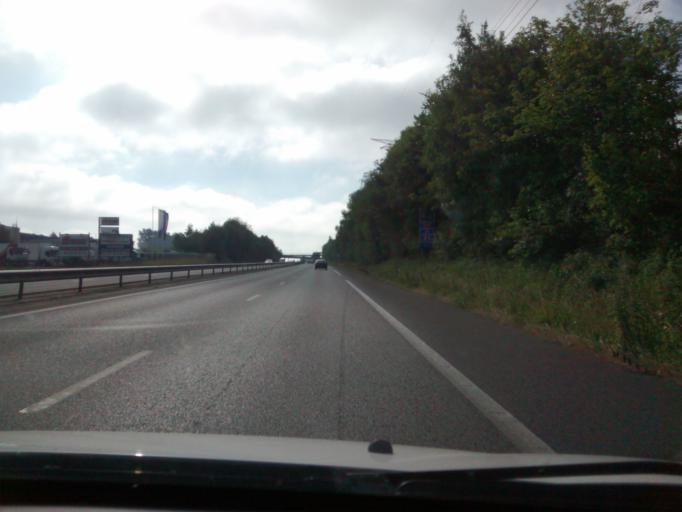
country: FR
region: Pays de la Loire
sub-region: Departement de la Mayenne
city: Saint-Pierre-la-Cour
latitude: 48.0847
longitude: -1.0515
